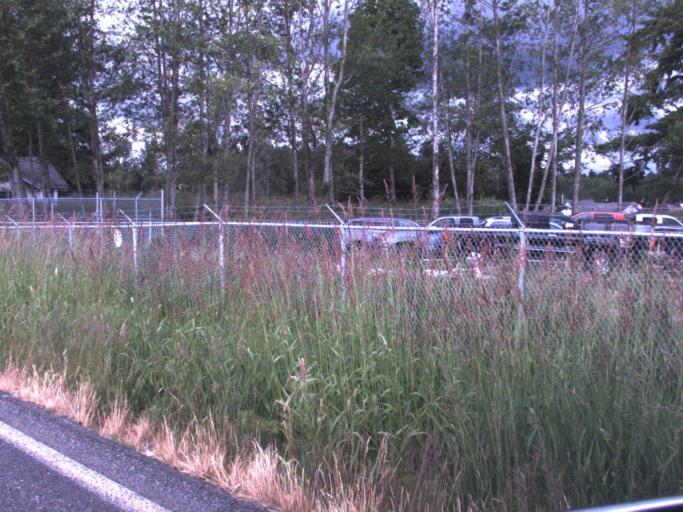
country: US
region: Washington
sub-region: Whatcom County
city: Birch Bay
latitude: 48.9336
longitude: -122.7263
